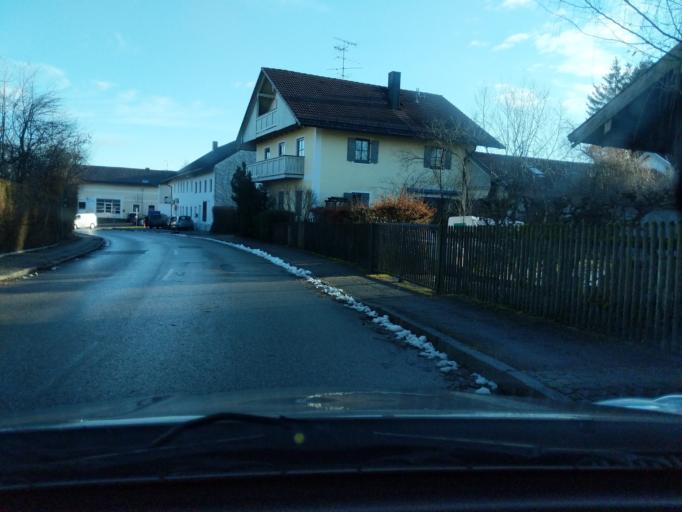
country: DE
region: Bavaria
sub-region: Upper Bavaria
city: Zorneding
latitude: 48.0953
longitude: 11.8319
